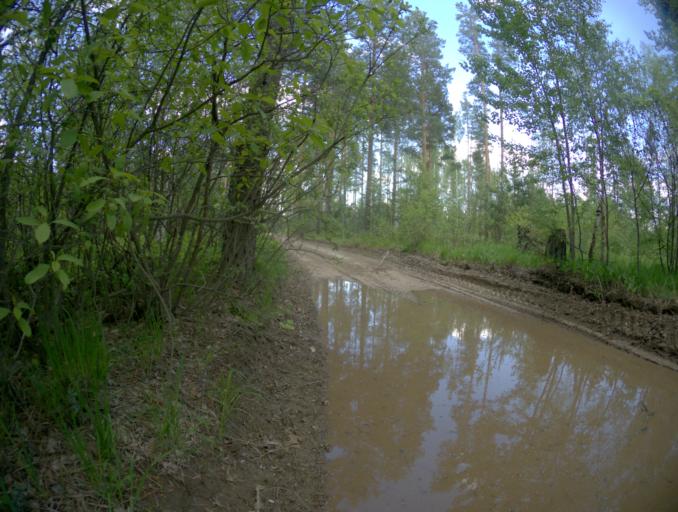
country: RU
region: Vladimir
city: Zolotkovo
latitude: 55.3289
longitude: 40.9527
